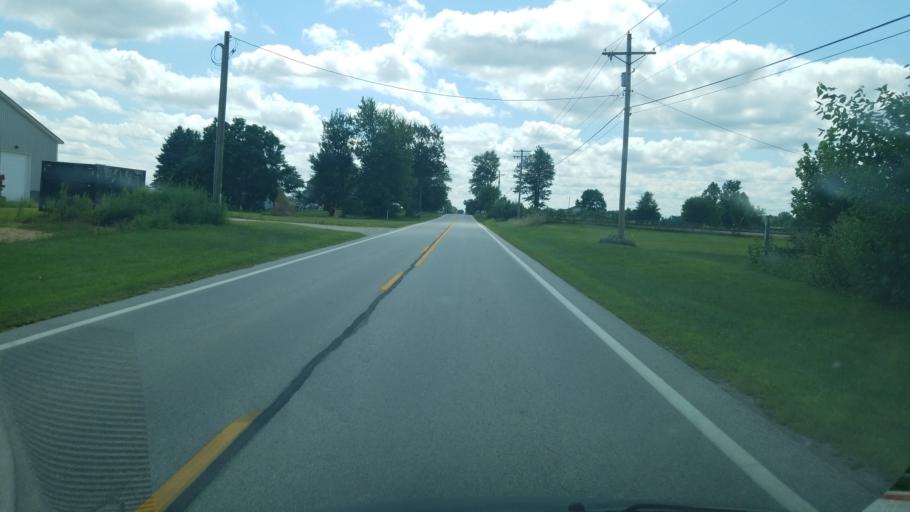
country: US
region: Ohio
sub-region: Henry County
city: Liberty Center
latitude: 41.4996
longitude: -84.0088
